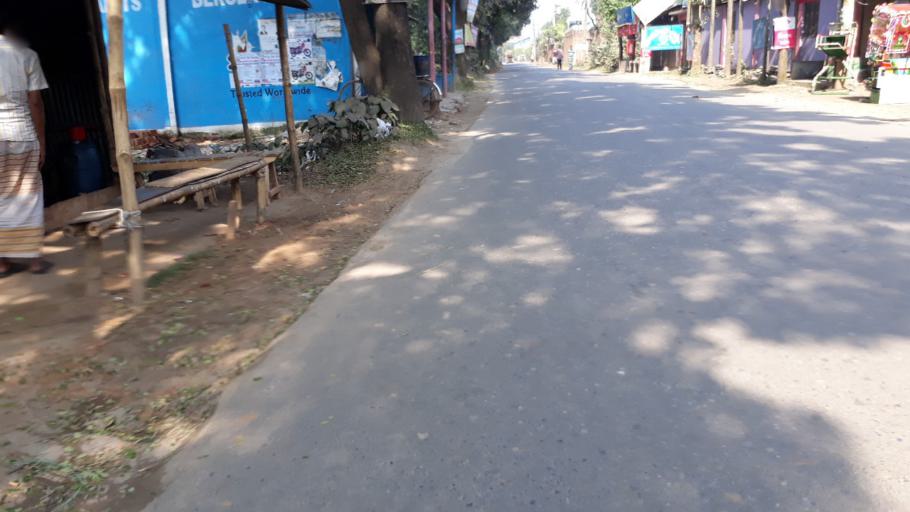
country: BD
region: Dhaka
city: Tungi
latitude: 23.8614
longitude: 90.3110
